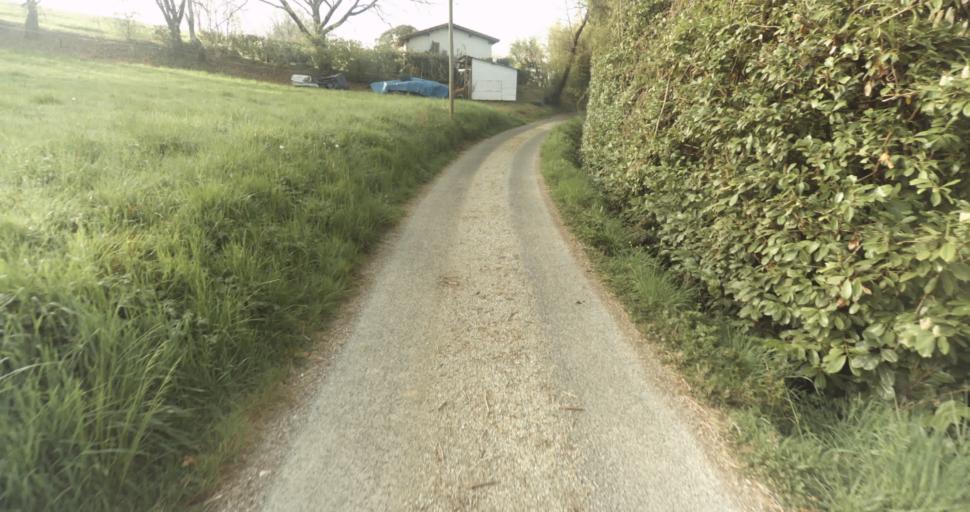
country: FR
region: Midi-Pyrenees
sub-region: Departement du Tarn-et-Garonne
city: Moissac
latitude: 44.1348
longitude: 1.1057
